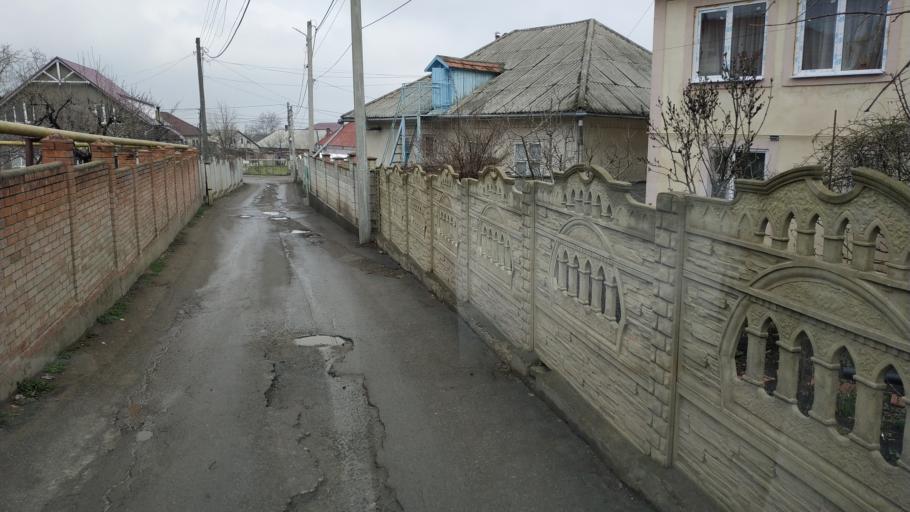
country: MD
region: Chisinau
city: Vatra
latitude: 47.0177
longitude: 28.7563
